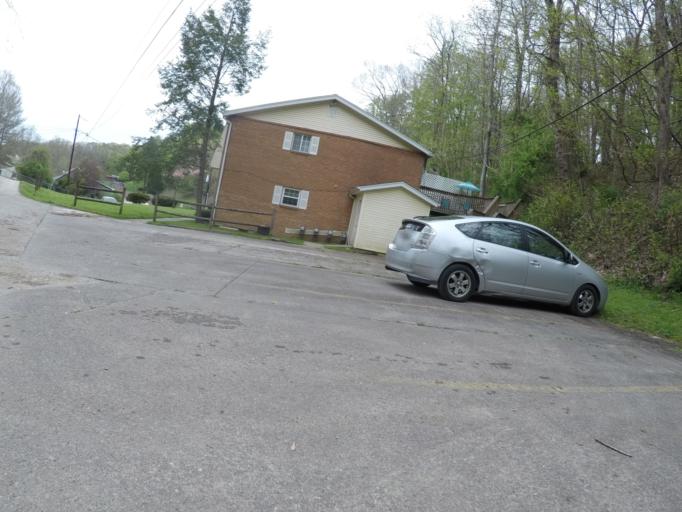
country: US
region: Ohio
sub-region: Lawrence County
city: Burlington
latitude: 38.3885
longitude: -82.5151
